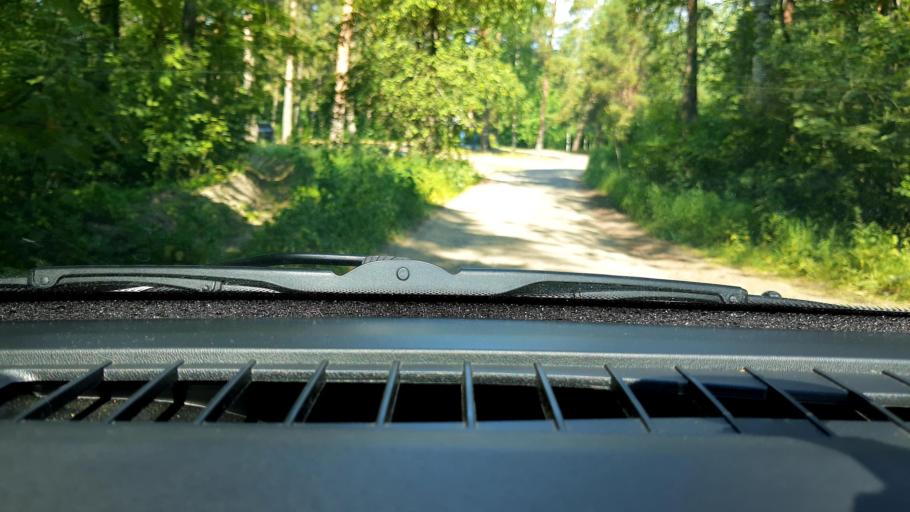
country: RU
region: Nizjnij Novgorod
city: Burevestnik
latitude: 56.1975
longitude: 43.7974
